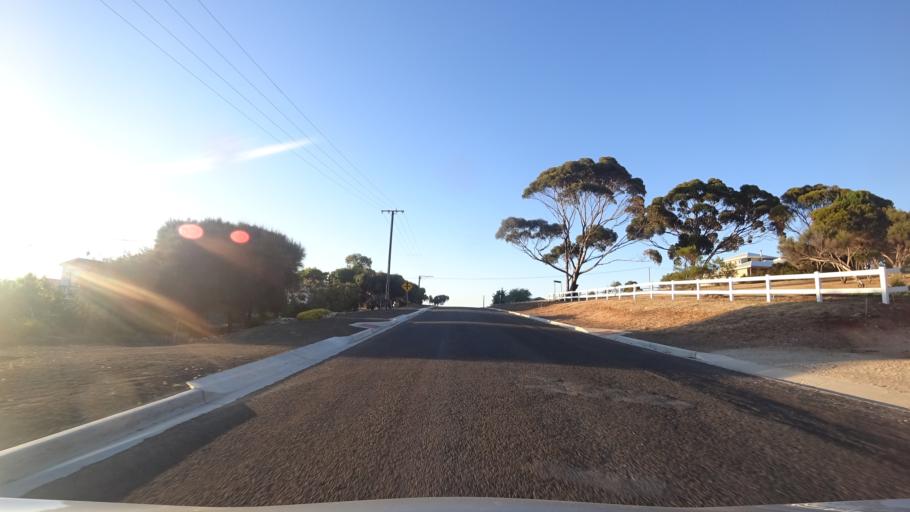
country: AU
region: South Australia
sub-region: Kangaroo Island
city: Kingscote
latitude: -35.6463
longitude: 137.6353
